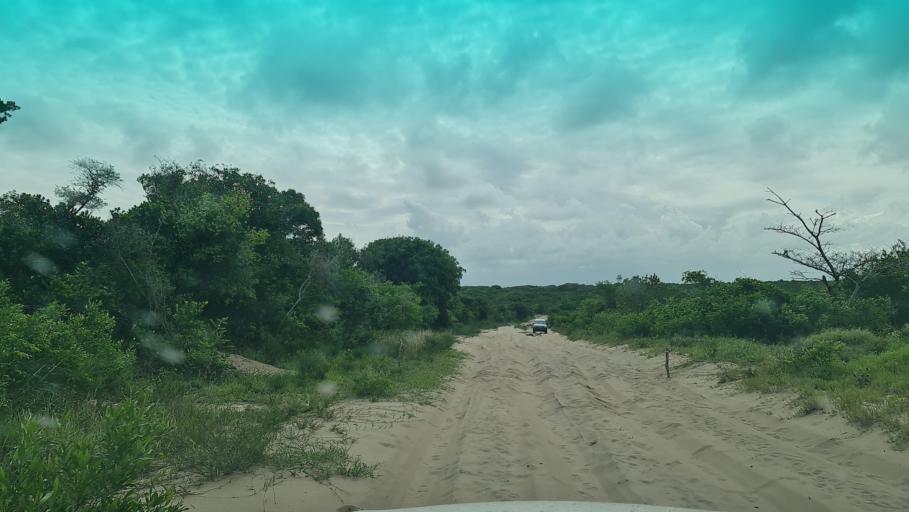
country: MZ
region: Maputo
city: Manhica
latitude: -25.4415
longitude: 32.9355
